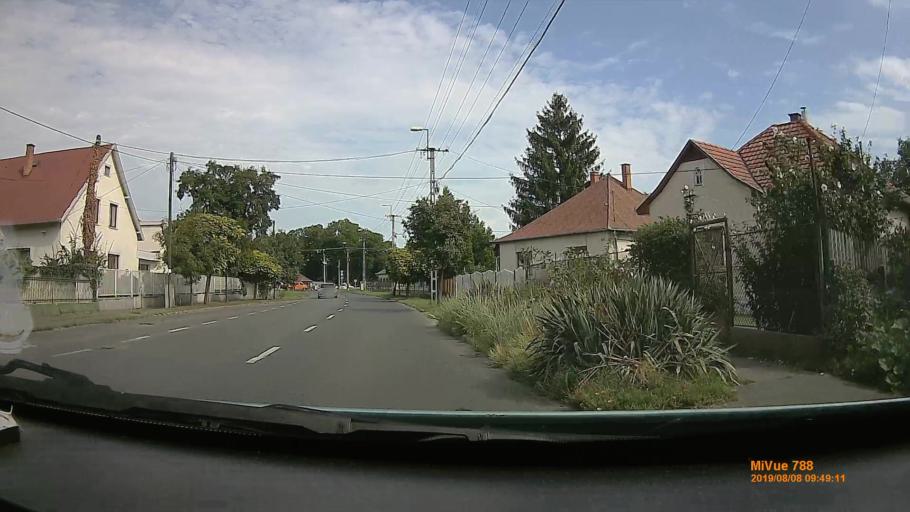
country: HU
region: Hajdu-Bihar
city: Debrecen
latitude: 47.5455
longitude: 21.6532
